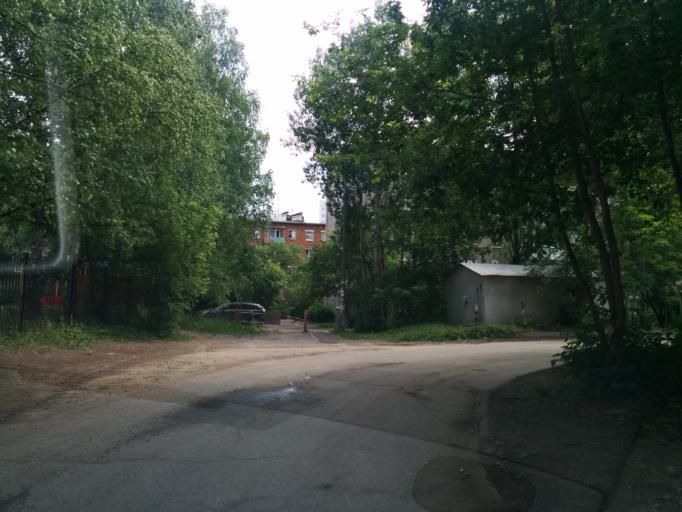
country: RU
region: Perm
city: Perm
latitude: 58.0153
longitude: 56.2976
